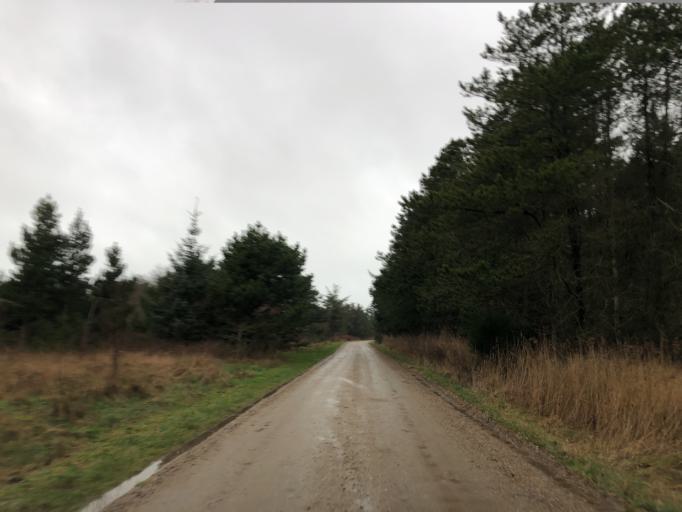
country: DK
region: Central Jutland
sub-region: Holstebro Kommune
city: Ulfborg
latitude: 56.2785
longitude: 8.1509
